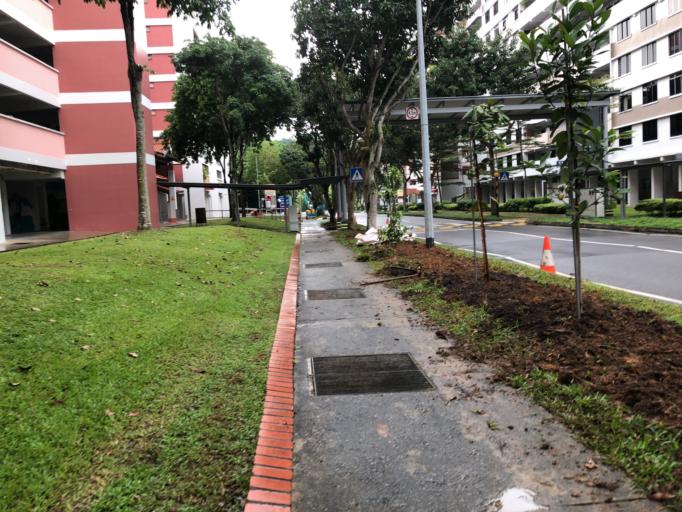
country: MY
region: Johor
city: Johor Bahru
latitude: 1.3556
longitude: 103.7511
